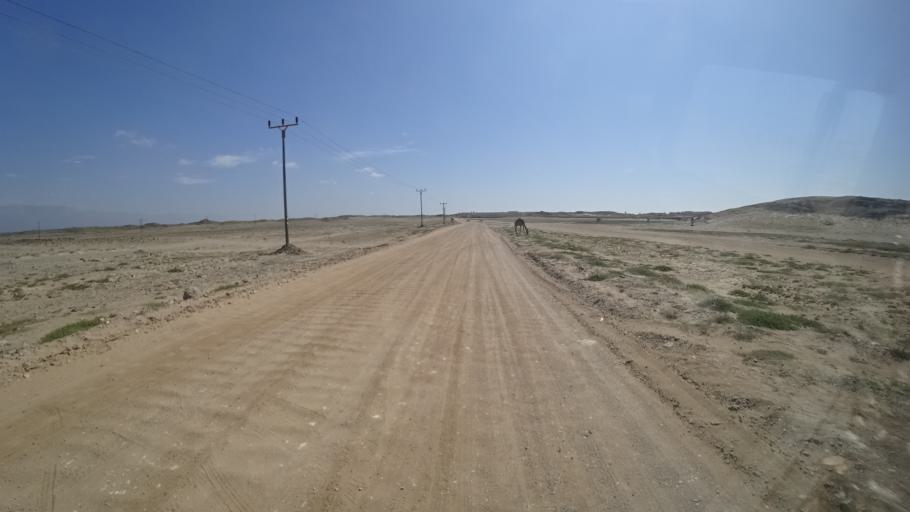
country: OM
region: Zufar
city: Salalah
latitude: 16.9629
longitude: 54.7684
